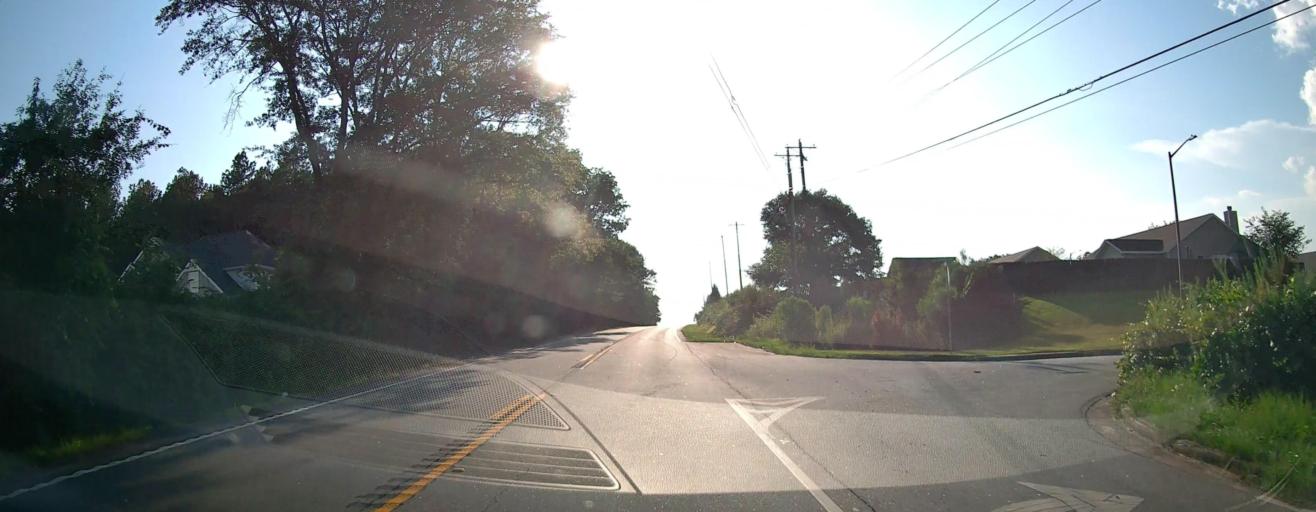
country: US
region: Georgia
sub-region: Houston County
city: Perry
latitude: 32.5060
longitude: -83.6449
